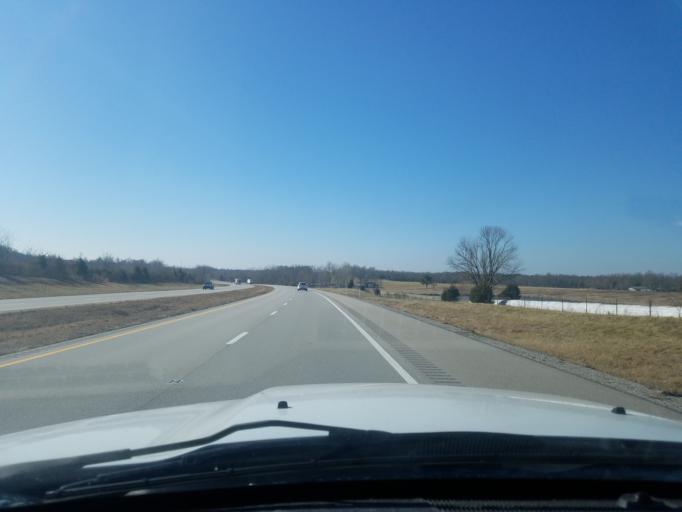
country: US
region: Kentucky
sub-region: Grayson County
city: Leitchfield
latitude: 37.4427
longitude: -86.3655
